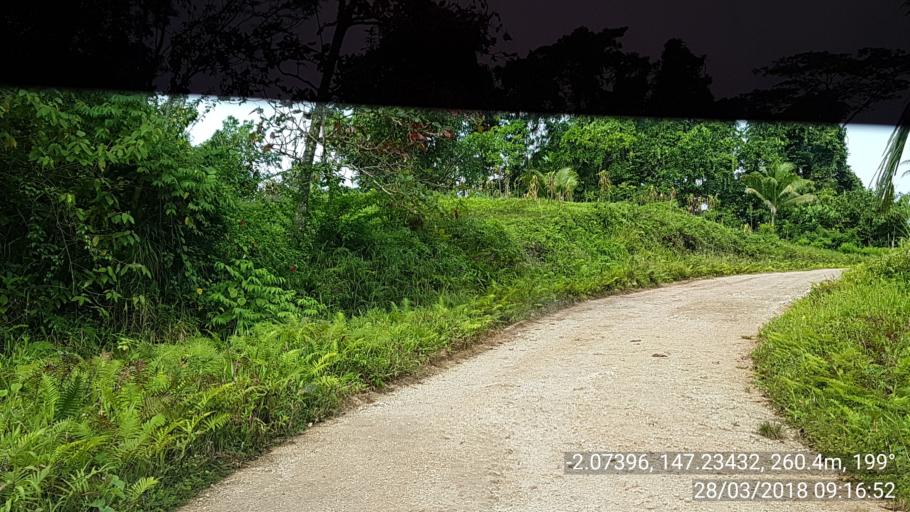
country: PG
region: Manus
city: Lorengau
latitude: -2.0739
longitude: 147.2344
